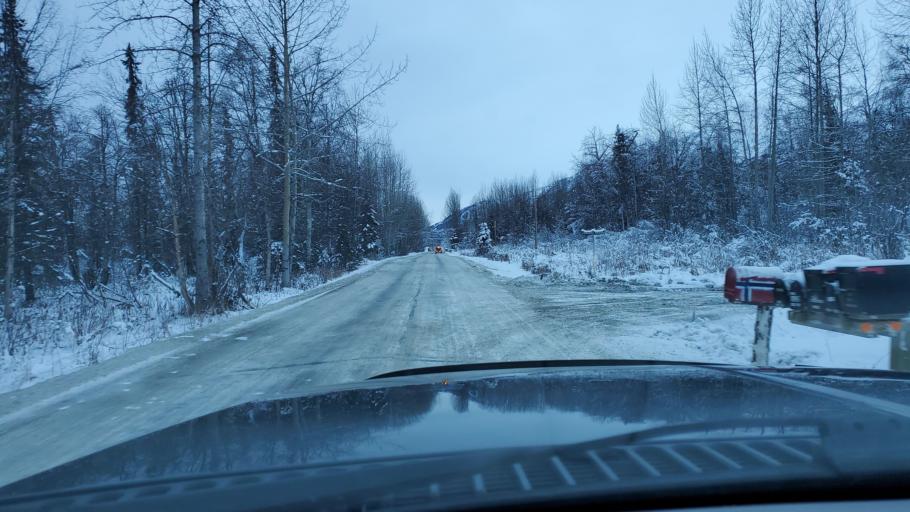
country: US
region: Alaska
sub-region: Matanuska-Susitna Borough
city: Fishhook
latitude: 61.6933
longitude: -149.3032
